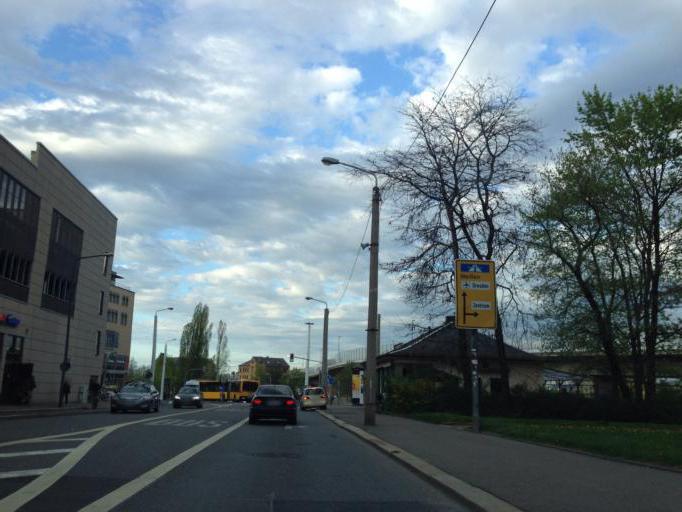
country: DE
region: Saxony
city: Dresden
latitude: 51.0428
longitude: 13.7038
